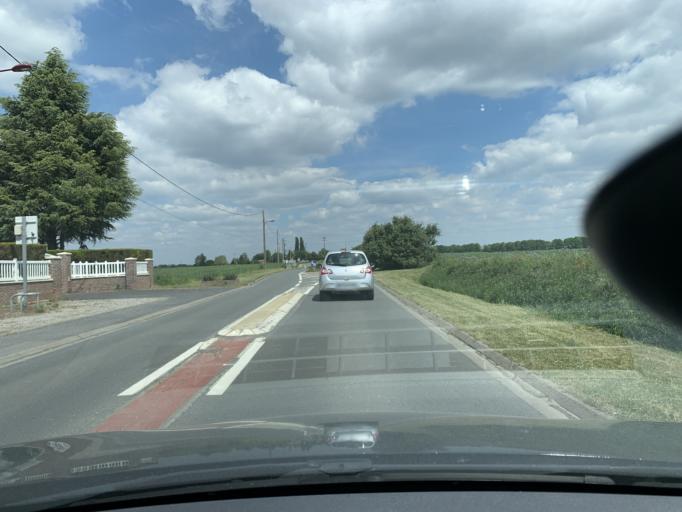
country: FR
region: Nord-Pas-de-Calais
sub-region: Departement du Nord
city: Goeulzin
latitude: 50.3240
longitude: 3.0949
